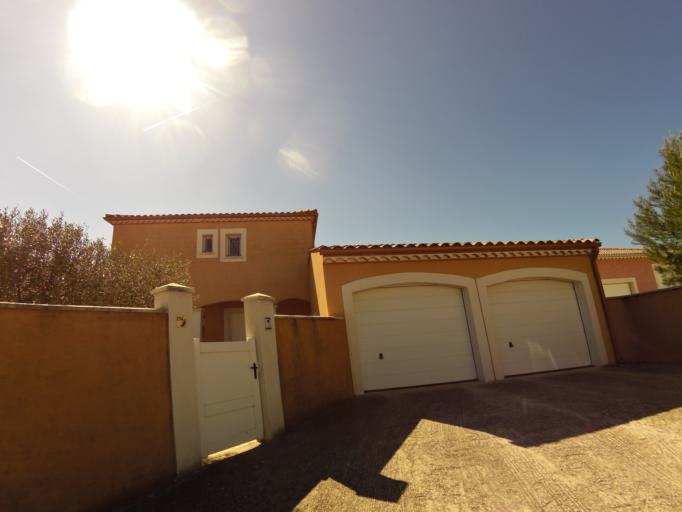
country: FR
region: Languedoc-Roussillon
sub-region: Departement du Gard
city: Sommieres
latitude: 43.8284
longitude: 4.0261
